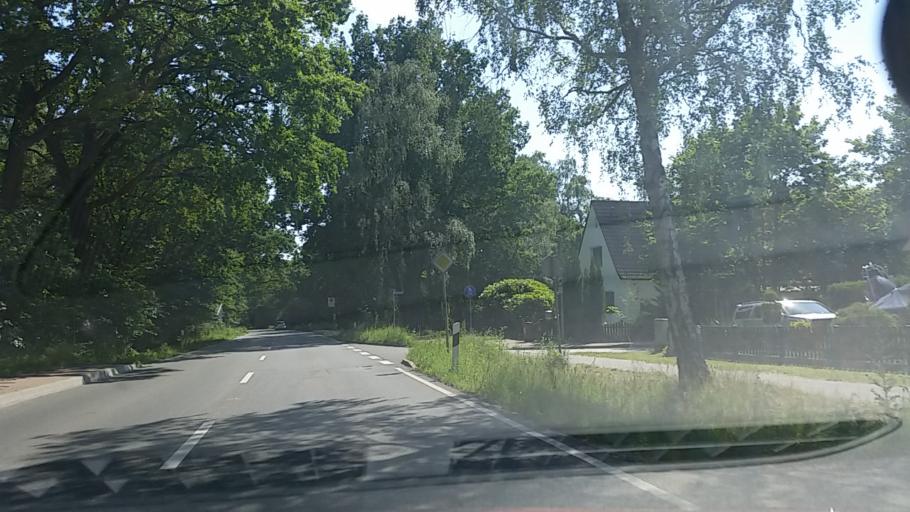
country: DE
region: Schleswig-Holstein
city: Reinbek
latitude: 53.5491
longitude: 10.2507
